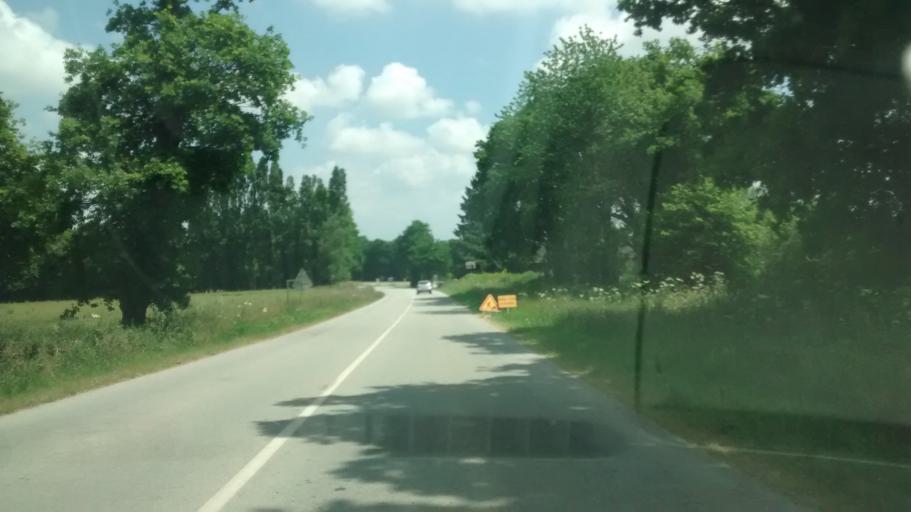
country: FR
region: Brittany
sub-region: Departement du Morbihan
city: Guer
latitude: 47.9027
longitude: -2.1400
